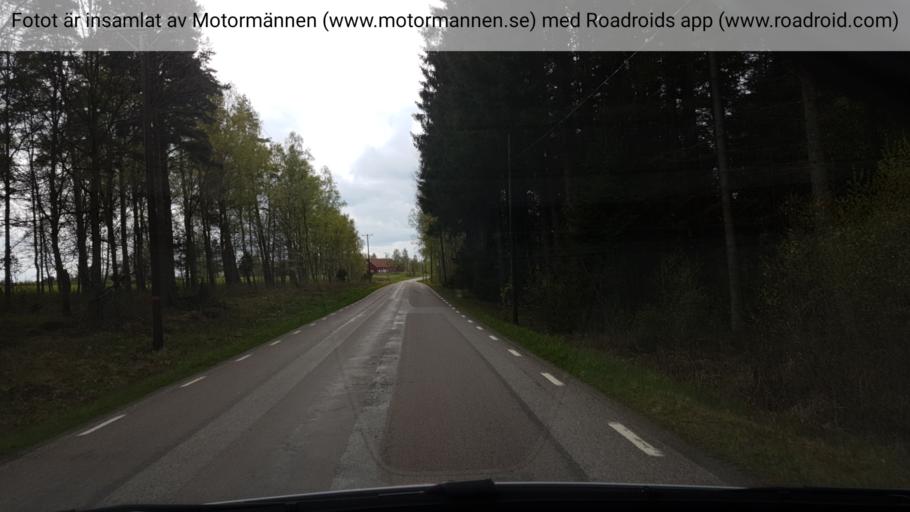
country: SE
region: Vaestra Goetaland
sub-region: Falkopings Kommun
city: Floby
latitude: 58.1686
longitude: 13.3432
